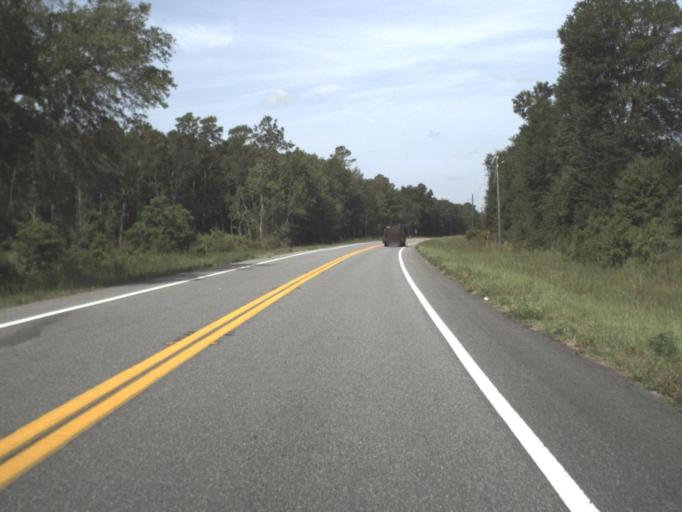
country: US
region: Florida
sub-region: Lafayette County
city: Mayo
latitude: 29.9730
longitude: -83.2083
